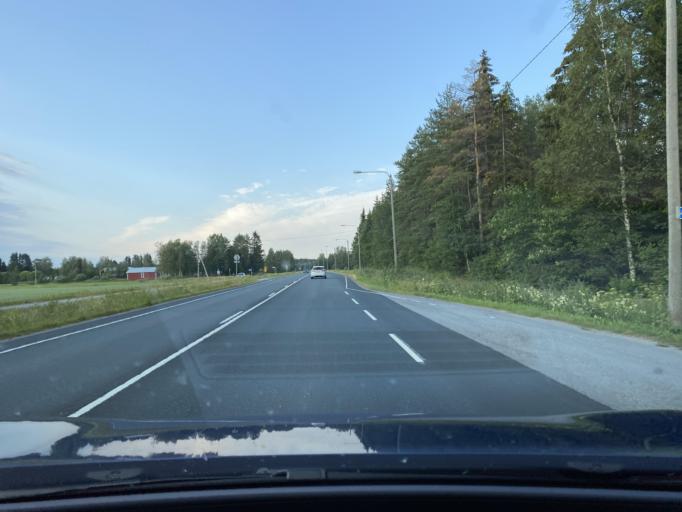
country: FI
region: Ostrobothnia
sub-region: Jakobstadsregionen
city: Bennaes
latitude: 63.6363
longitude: 22.8692
